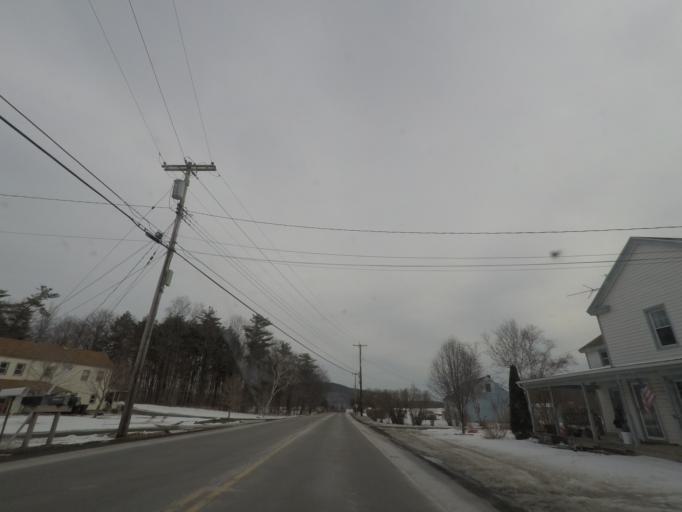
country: US
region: New York
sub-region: Albany County
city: Voorheesville
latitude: 42.5788
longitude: -73.9779
